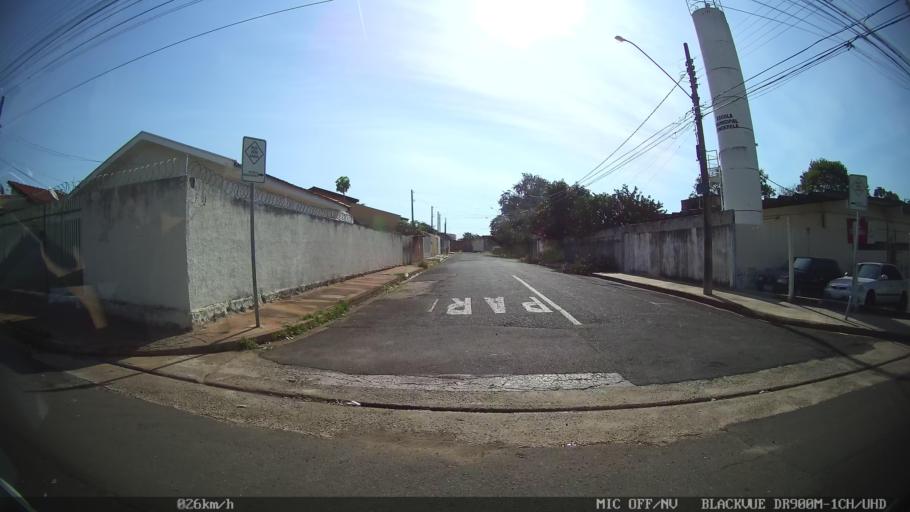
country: BR
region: Sao Paulo
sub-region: Sao Jose Do Rio Preto
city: Sao Jose do Rio Preto
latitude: -20.7919
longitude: -49.3804
